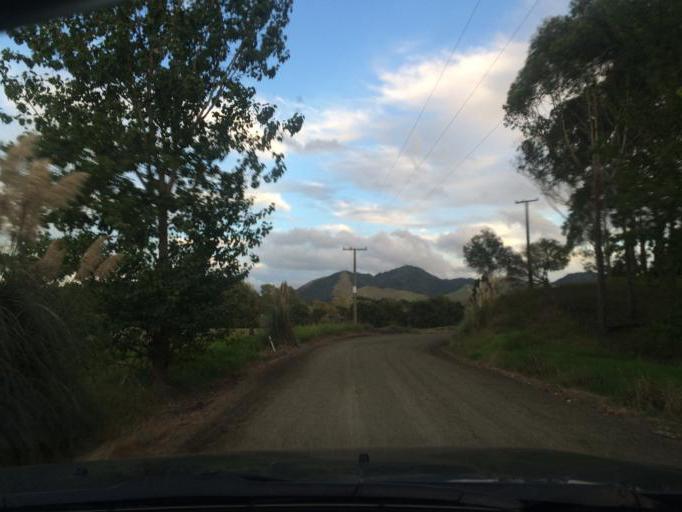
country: NZ
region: Northland
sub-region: Whangarei
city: Maungatapere
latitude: -35.8179
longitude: 174.0395
